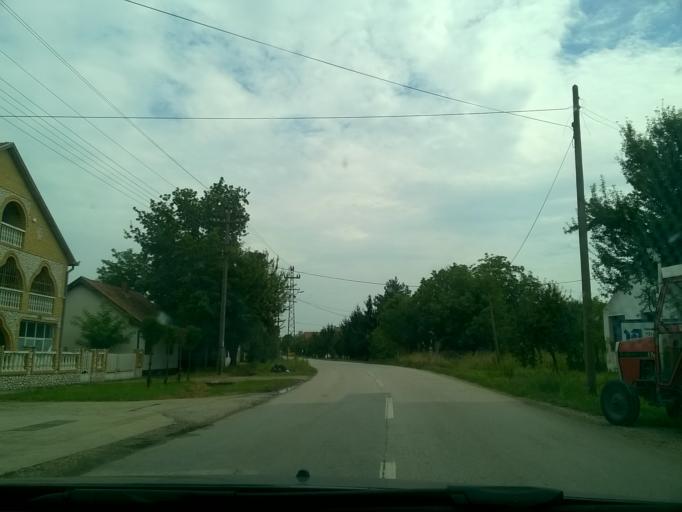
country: RS
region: Autonomna Pokrajina Vojvodina
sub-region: Srednjebanatski Okrug
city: Secanj
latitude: 45.3672
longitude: 20.7664
